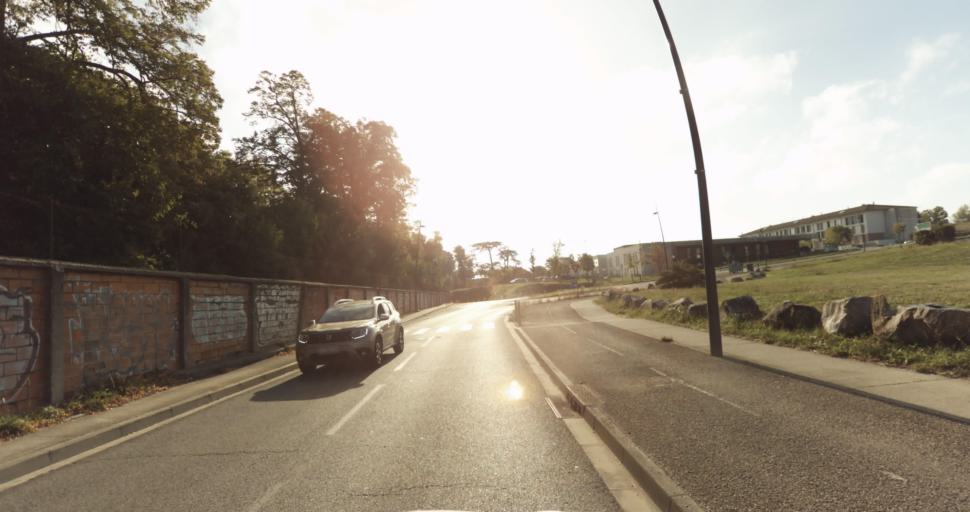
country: FR
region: Midi-Pyrenees
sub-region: Departement de la Haute-Garonne
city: Ramonville-Saint-Agne
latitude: 43.5370
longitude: 1.4681
